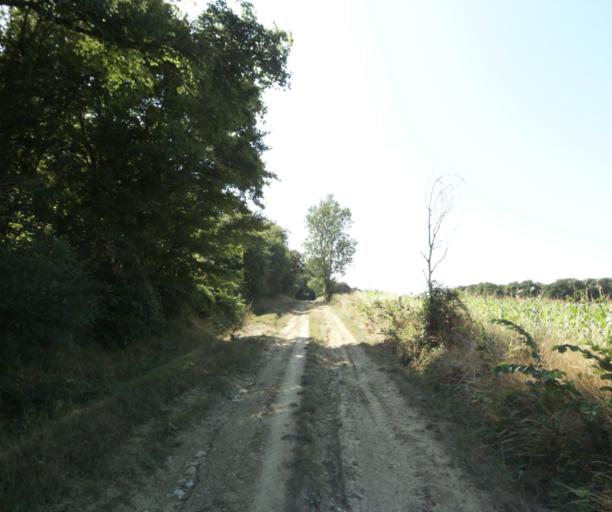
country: FR
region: Midi-Pyrenees
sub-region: Departement de la Haute-Garonne
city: Saint-Felix-Lauragais
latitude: 43.4563
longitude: 1.8591
